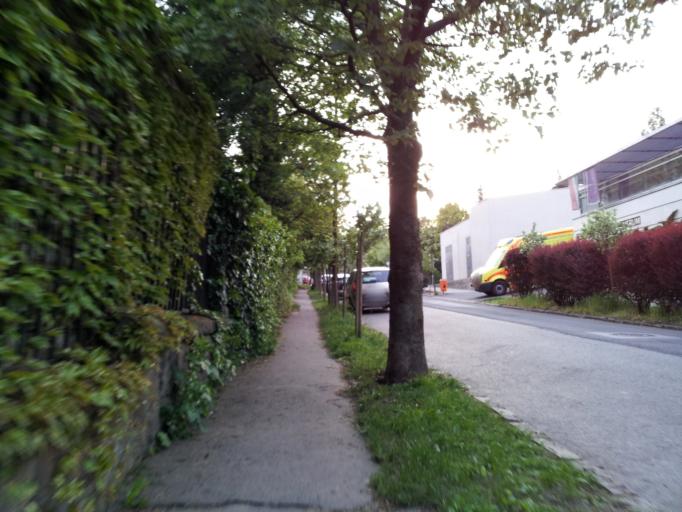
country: HU
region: Budapest
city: Budapest XII. keruelet
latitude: 47.5064
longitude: 19.0134
